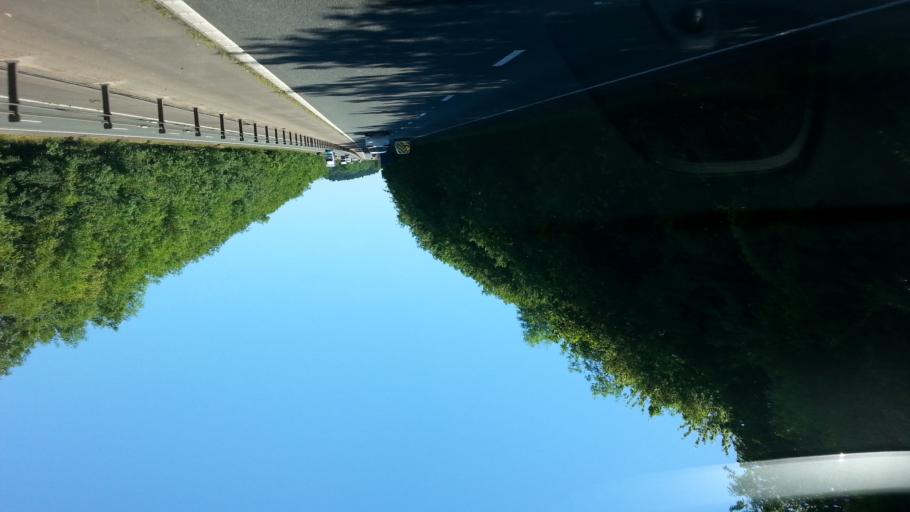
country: GB
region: Wales
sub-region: Newport
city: Langstone
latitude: 51.6294
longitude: -2.8958
